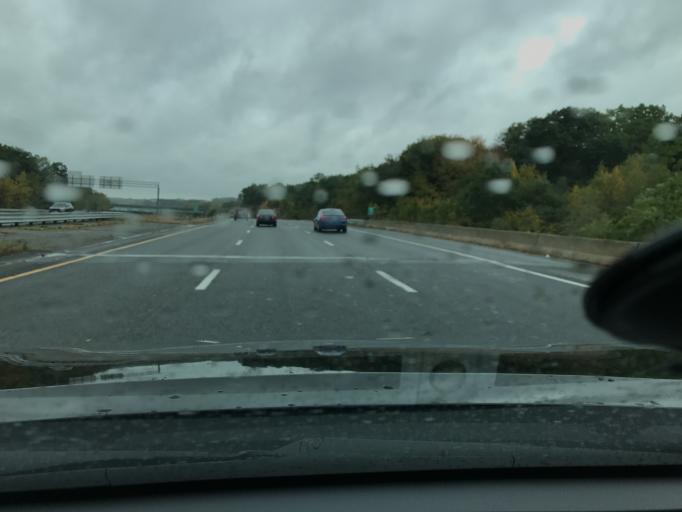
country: US
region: Massachusetts
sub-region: Essex County
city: South Peabody
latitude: 42.5259
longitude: -70.9714
